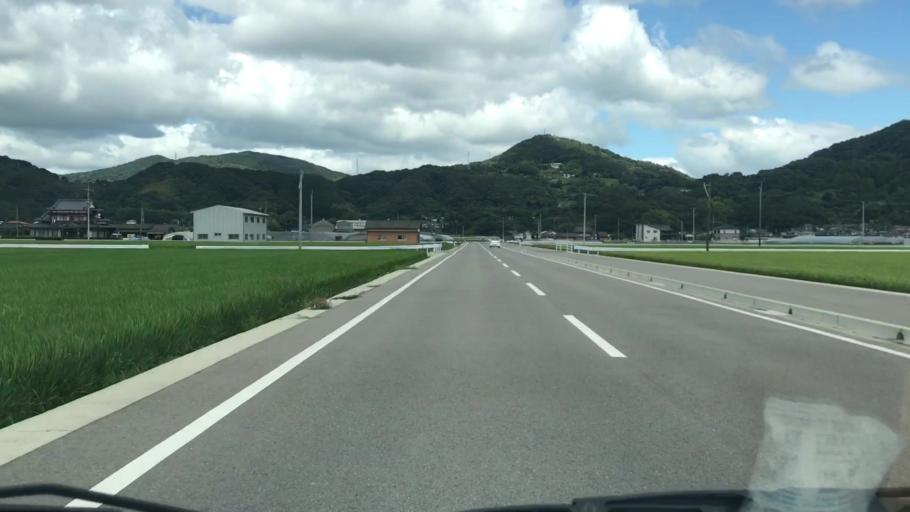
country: JP
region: Saga Prefecture
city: Kashima
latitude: 33.2208
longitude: 130.1451
